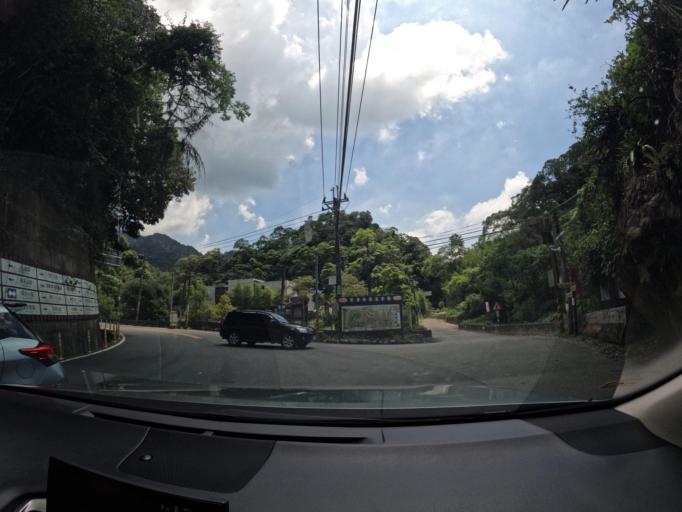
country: TW
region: Taiwan
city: Fengyuan
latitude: 24.3912
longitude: 120.7945
